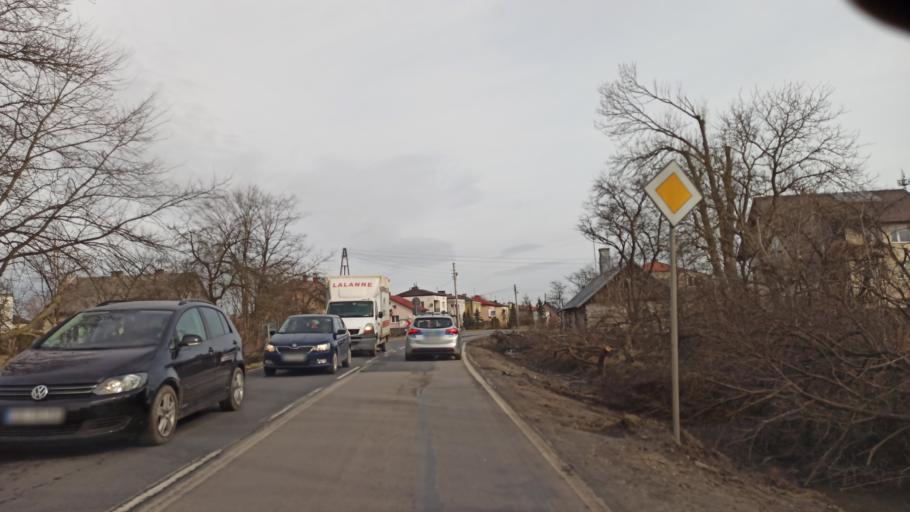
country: PL
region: Lublin Voivodeship
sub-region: Powiat bilgorajski
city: Tarnogrod
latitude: 50.3495
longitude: 22.7347
